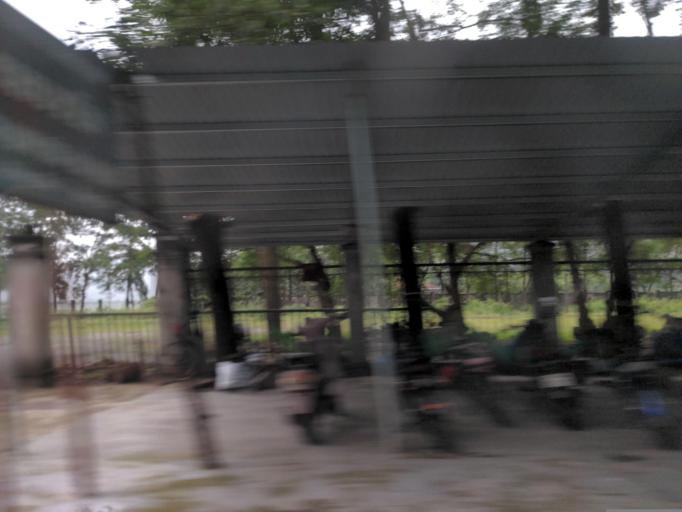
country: VN
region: Ninh Binh
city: Thi Tran Tam Diep
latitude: 20.2093
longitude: 105.9077
